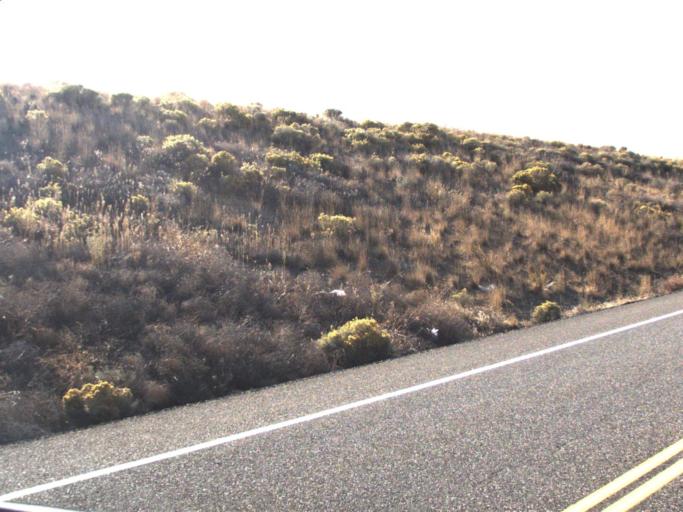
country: US
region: Washington
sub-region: Benton County
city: Highland
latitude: 46.1492
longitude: -119.1239
